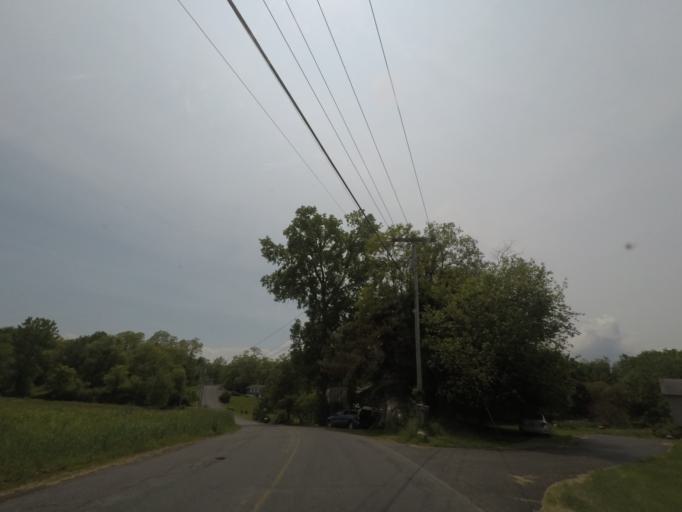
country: US
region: New York
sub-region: Rensselaer County
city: Castleton-on-Hudson
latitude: 42.5336
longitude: -73.7128
